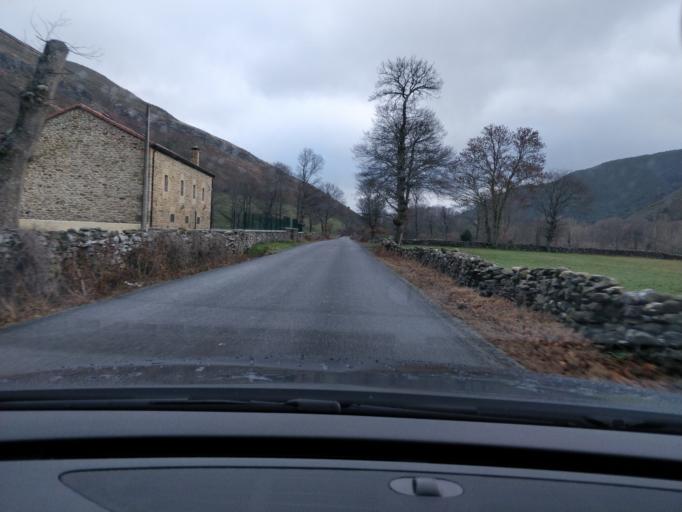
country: ES
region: Castille and Leon
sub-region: Provincia de Burgos
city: Espinosa de los Monteros
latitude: 43.1071
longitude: -3.5747
